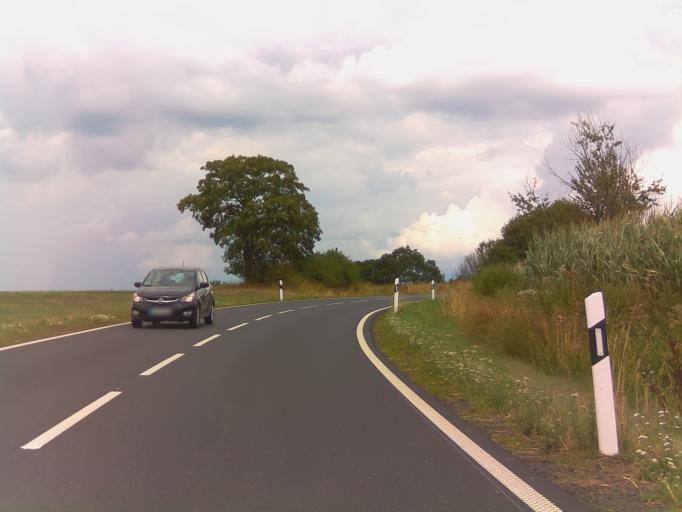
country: DE
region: Hesse
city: Gedern
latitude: 50.4122
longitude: 9.1964
